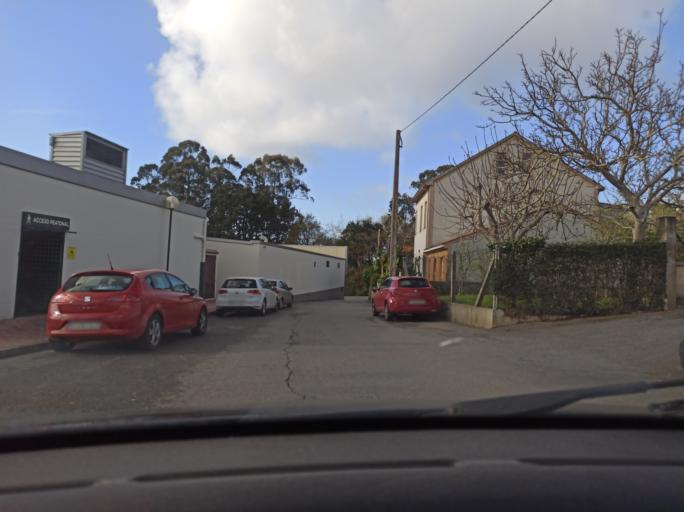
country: ES
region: Galicia
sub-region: Provincia da Coruna
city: Oleiros
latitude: 43.3329
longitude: -8.3051
